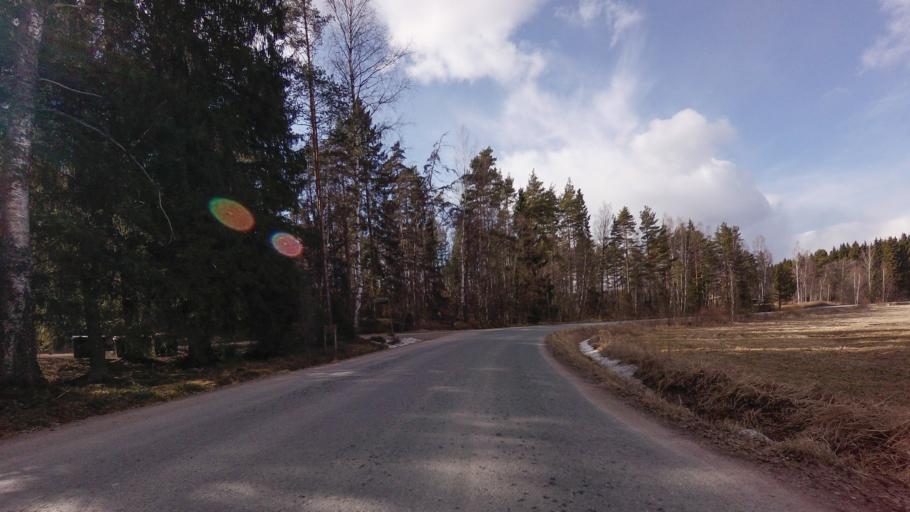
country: FI
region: Varsinais-Suomi
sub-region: Salo
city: Suomusjaervi
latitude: 60.3405
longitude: 23.6954
